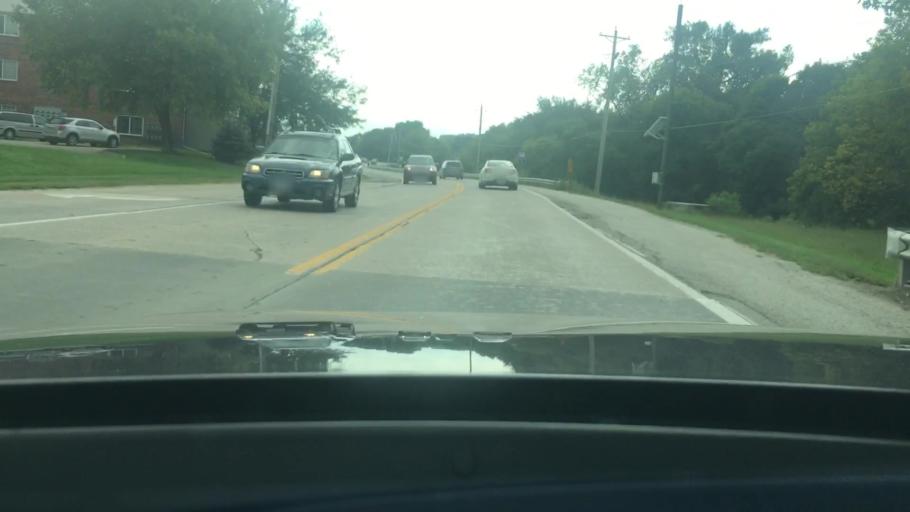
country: US
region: Iowa
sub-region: Pottawattamie County
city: Council Bluffs
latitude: 41.2536
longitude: -95.8109
